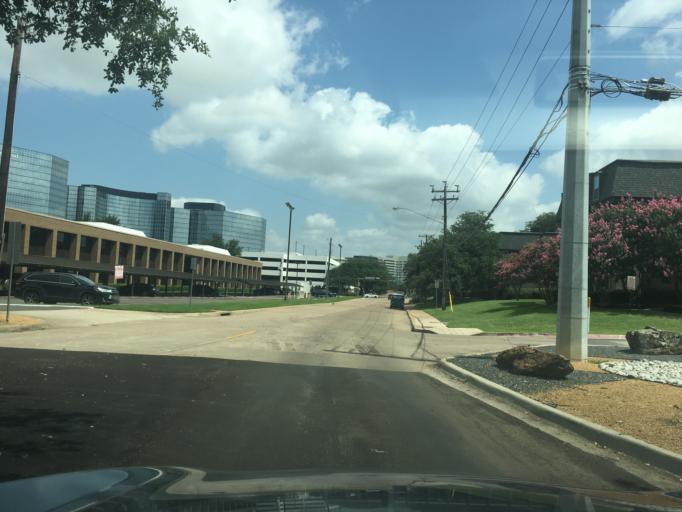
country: US
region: Texas
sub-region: Dallas County
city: Addison
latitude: 32.9203
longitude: -96.8149
